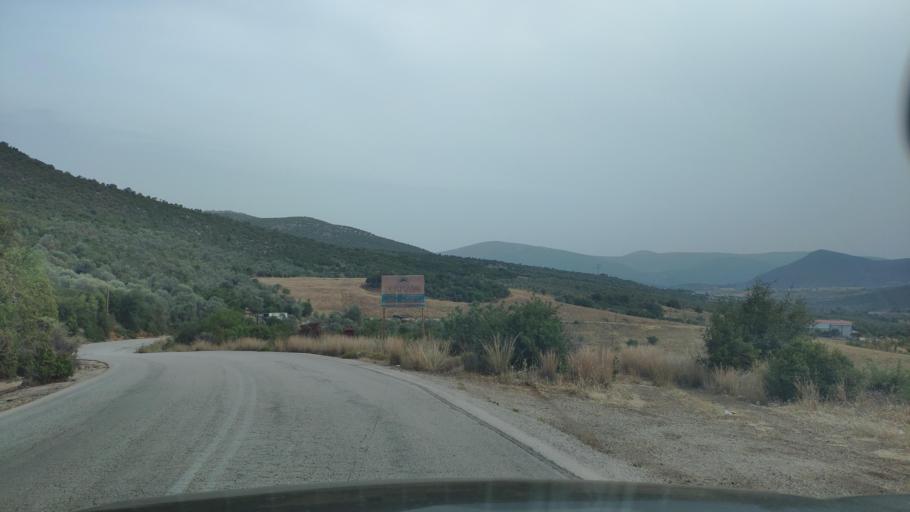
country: GR
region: Peloponnese
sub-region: Nomos Argolidos
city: Palaia Epidavros
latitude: 37.5828
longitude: 23.1536
